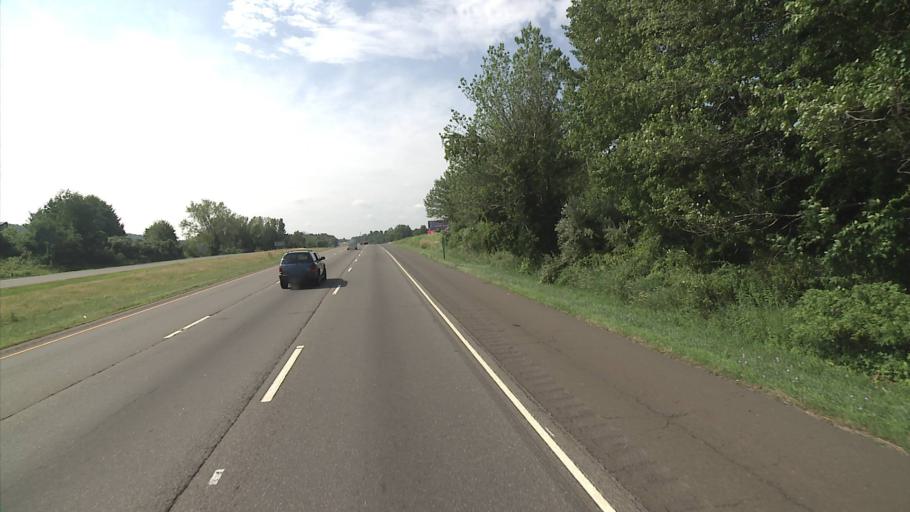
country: US
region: Connecticut
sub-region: New Haven County
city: Meriden
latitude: 41.5095
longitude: -72.7697
